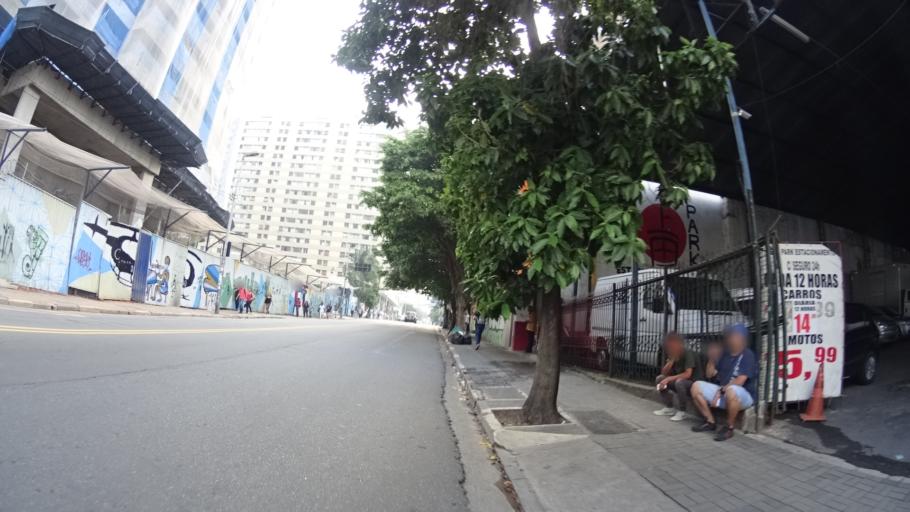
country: BR
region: Sao Paulo
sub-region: Sao Paulo
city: Sao Paulo
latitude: -23.5503
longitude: -46.6472
